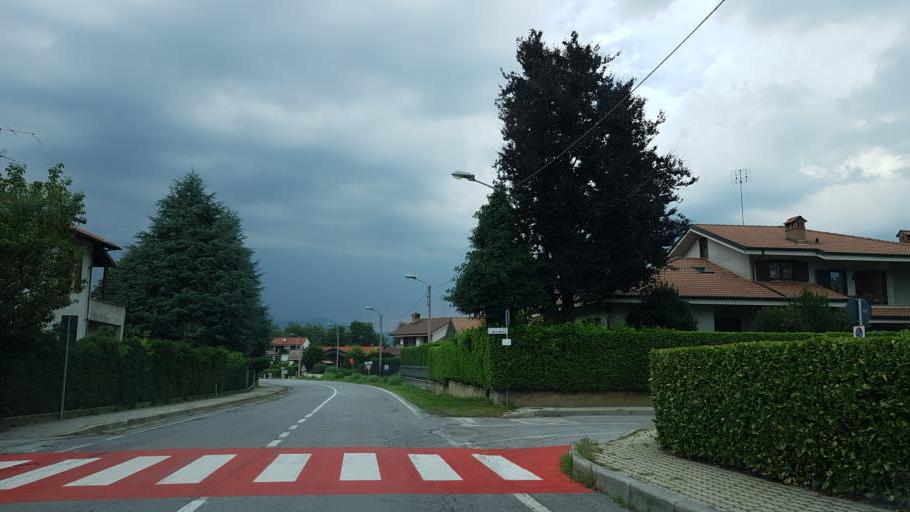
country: IT
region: Piedmont
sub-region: Provincia di Cuneo
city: Cervasca
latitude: 44.3836
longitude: 7.4674
